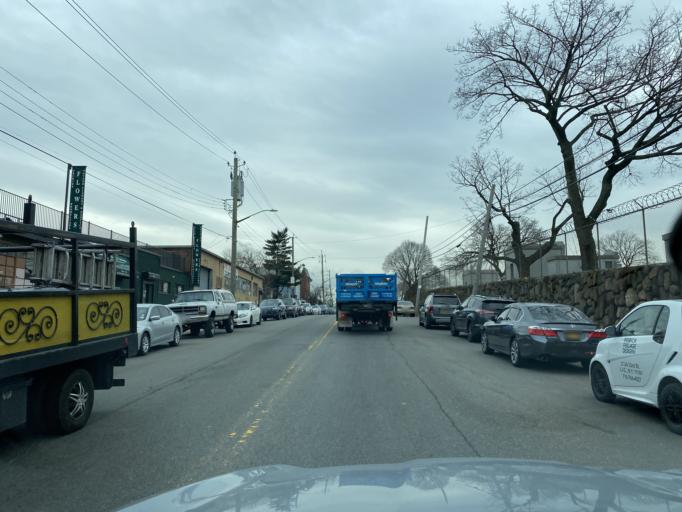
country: US
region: New York
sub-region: Queens County
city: Long Island City
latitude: 40.7399
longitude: -73.9081
